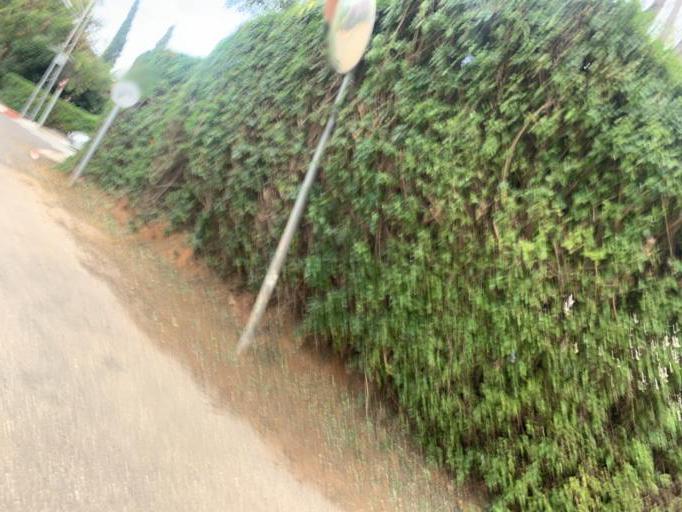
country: IL
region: Central District
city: Hod HaSharon
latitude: 32.1644
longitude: 34.8836
